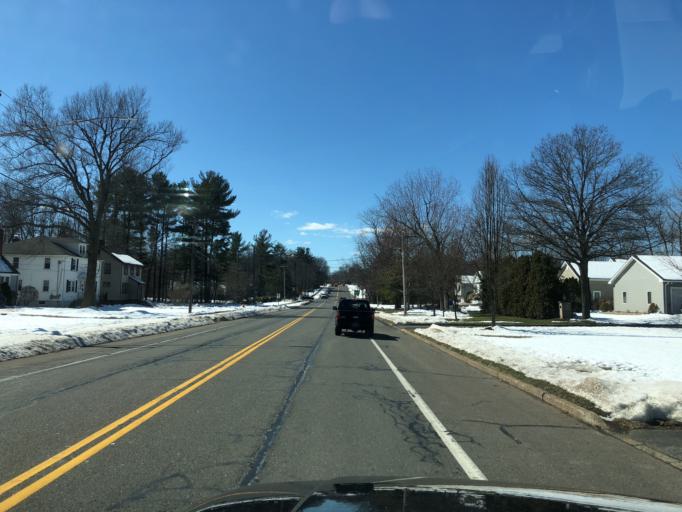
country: US
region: Connecticut
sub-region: Hartford County
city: Newington
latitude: 41.6843
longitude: -72.7284
